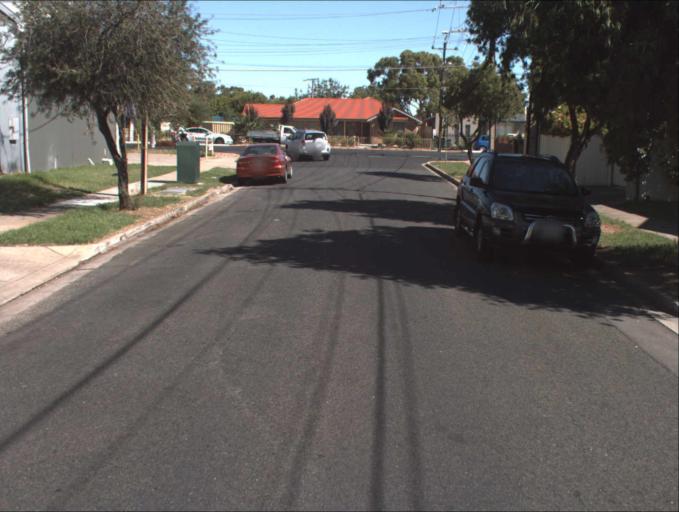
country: AU
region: South Australia
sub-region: Port Adelaide Enfield
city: Blair Athol
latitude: -34.8725
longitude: 138.6133
